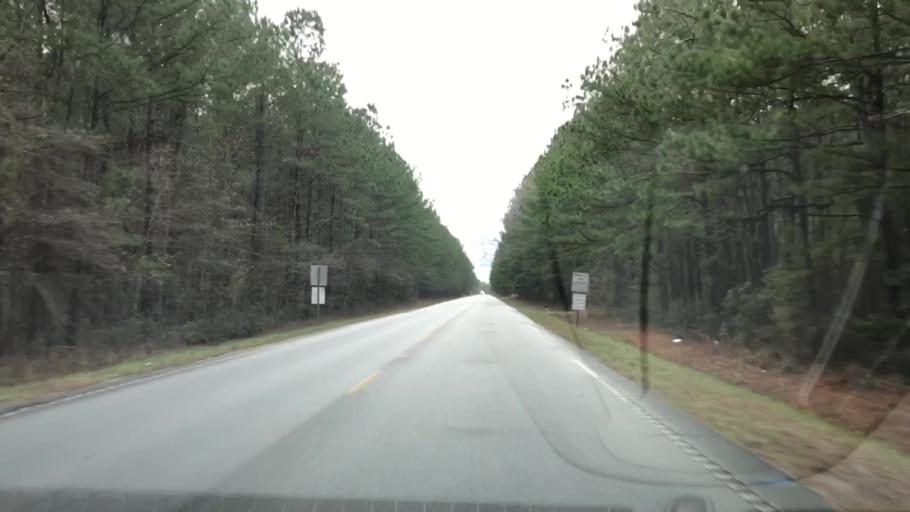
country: US
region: South Carolina
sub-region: Williamsburg County
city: Andrews
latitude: 33.2839
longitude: -79.7162
